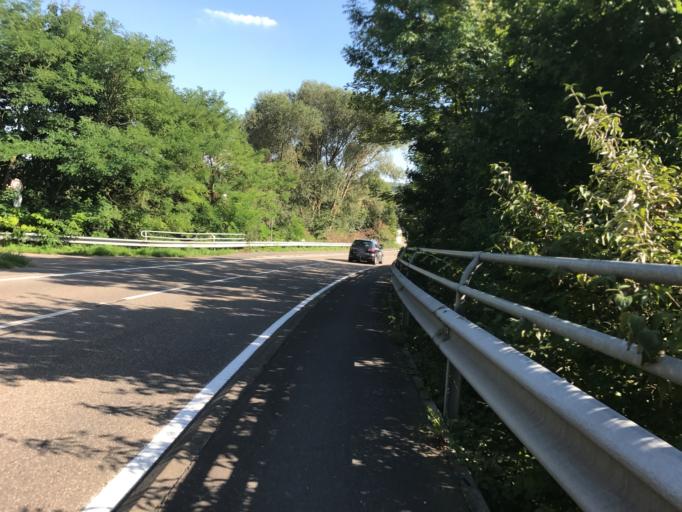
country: DE
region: Rheinland-Pfalz
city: Wackernheim
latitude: 50.0000
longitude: 8.1069
